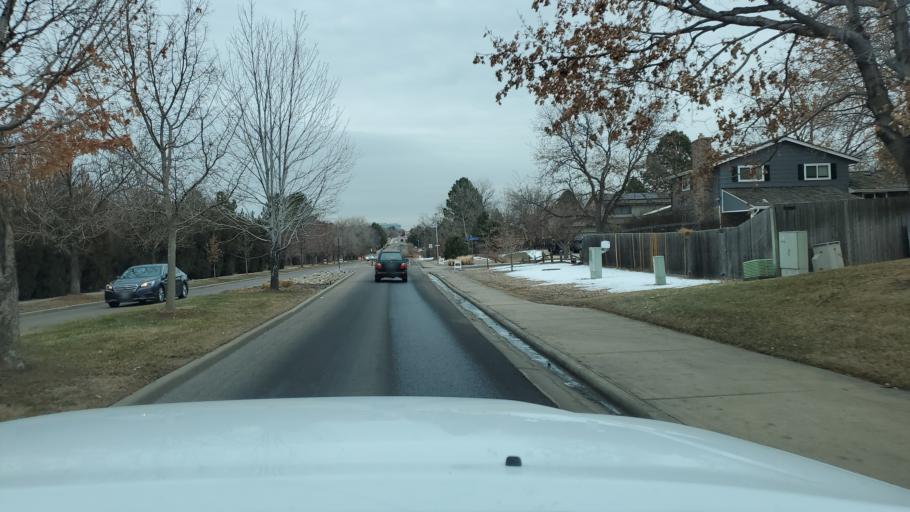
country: US
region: Colorado
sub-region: Arapahoe County
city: Castlewood
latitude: 39.6095
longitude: -104.9197
